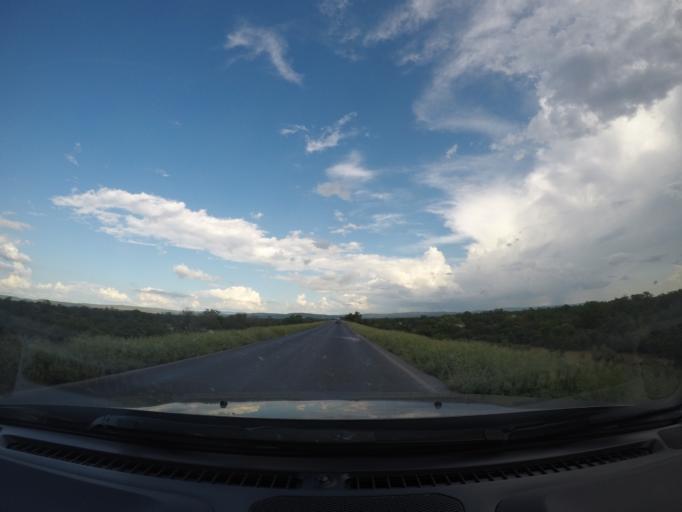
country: BR
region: Bahia
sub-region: Ibotirama
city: Ibotirama
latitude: -12.1673
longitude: -43.2735
